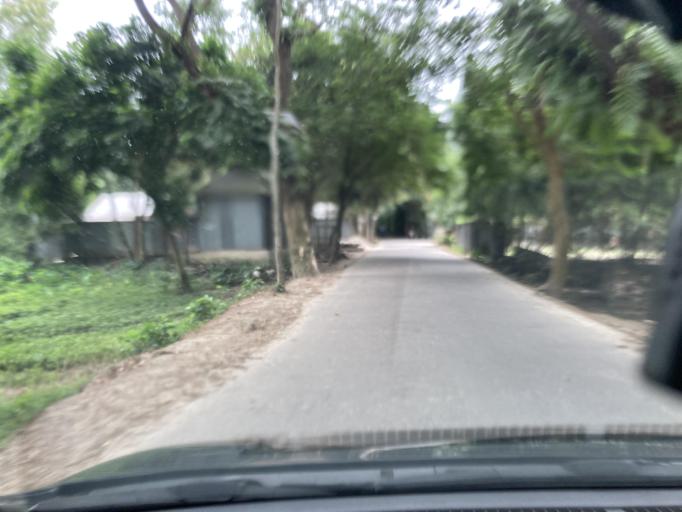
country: BD
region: Dhaka
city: Dohar
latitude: 23.7938
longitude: 90.0533
